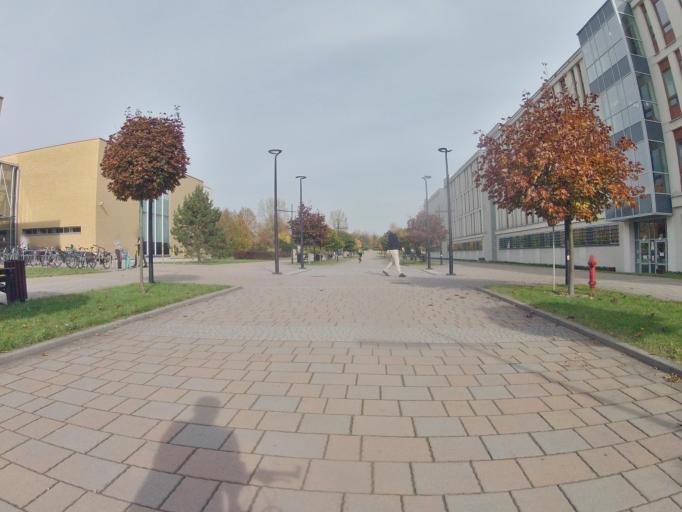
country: PL
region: Lesser Poland Voivodeship
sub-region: Krakow
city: Krakow
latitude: 50.0301
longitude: 19.9075
